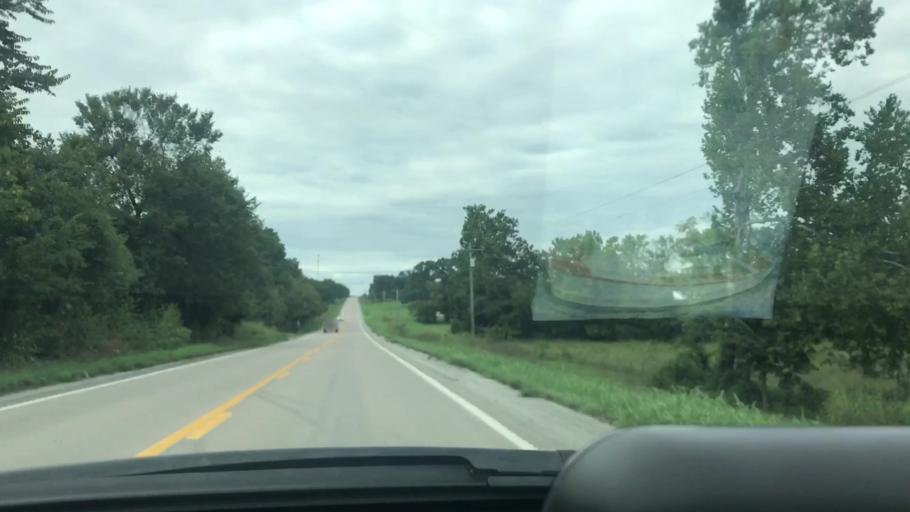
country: US
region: Missouri
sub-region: Benton County
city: Warsaw
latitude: 38.1343
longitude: -93.2814
